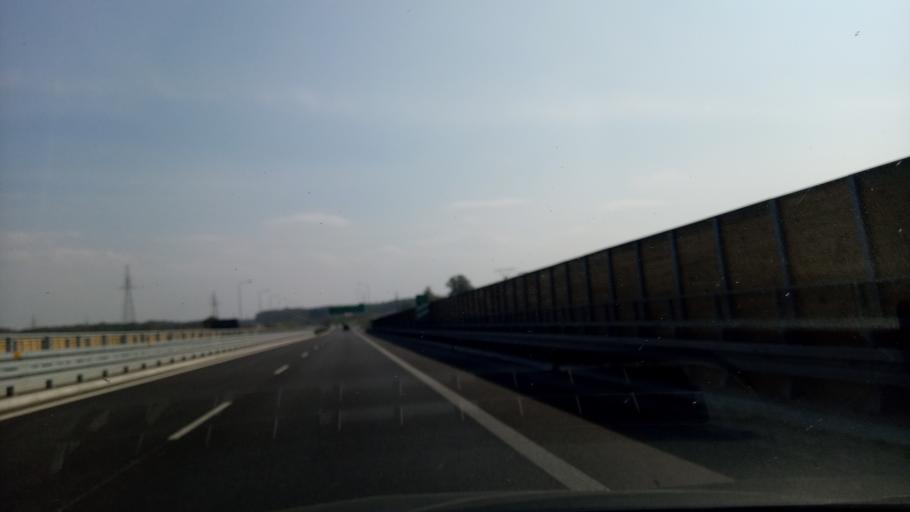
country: PL
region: West Pomeranian Voivodeship
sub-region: Powiat szczecinecki
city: Szczecinek
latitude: 53.6966
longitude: 16.7301
